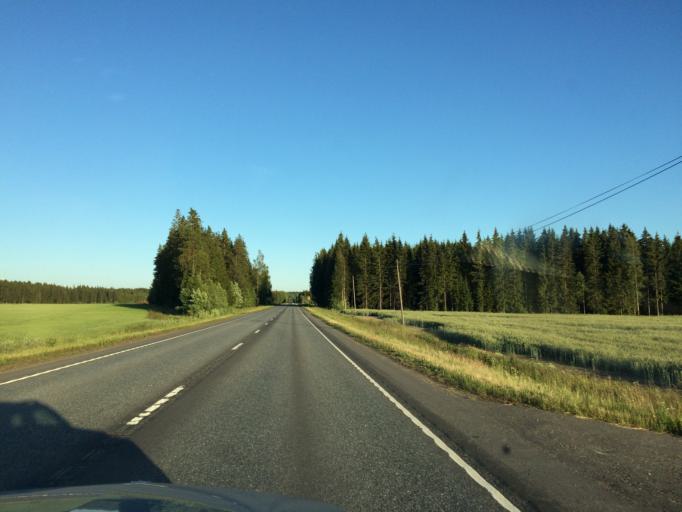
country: FI
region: Haeme
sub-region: Haemeenlinna
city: Tervakoski
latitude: 60.7854
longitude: 24.6830
